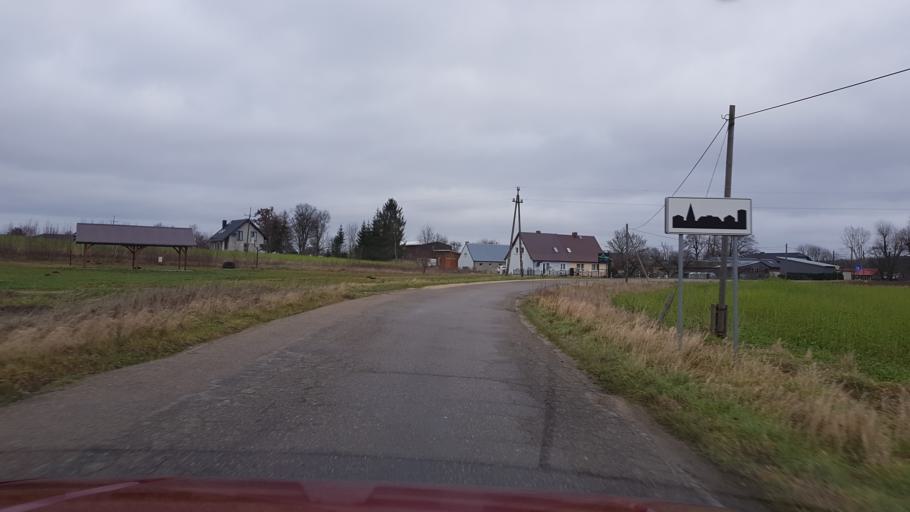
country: PL
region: Pomeranian Voivodeship
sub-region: Powiat bytowski
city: Borzytuchom
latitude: 54.1780
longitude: 17.3580
